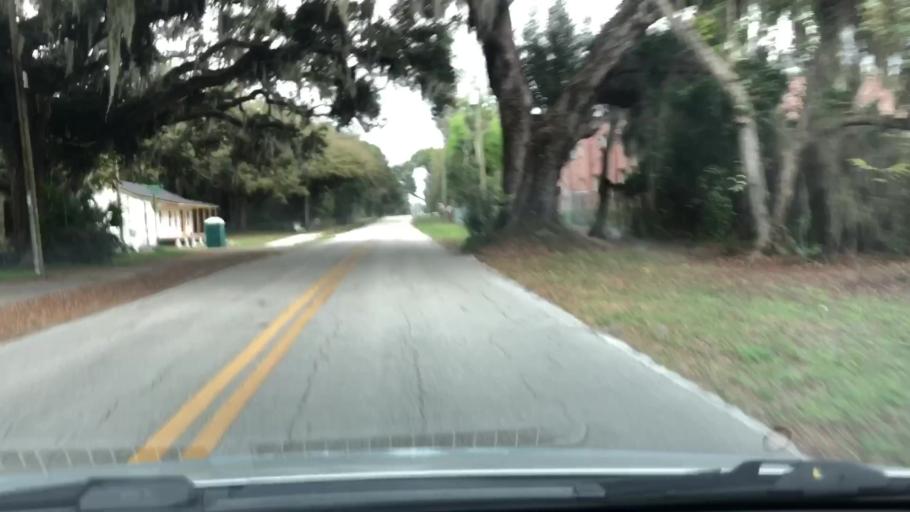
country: US
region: Florida
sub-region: Volusia County
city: Deltona
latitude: 28.8694
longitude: -81.2641
